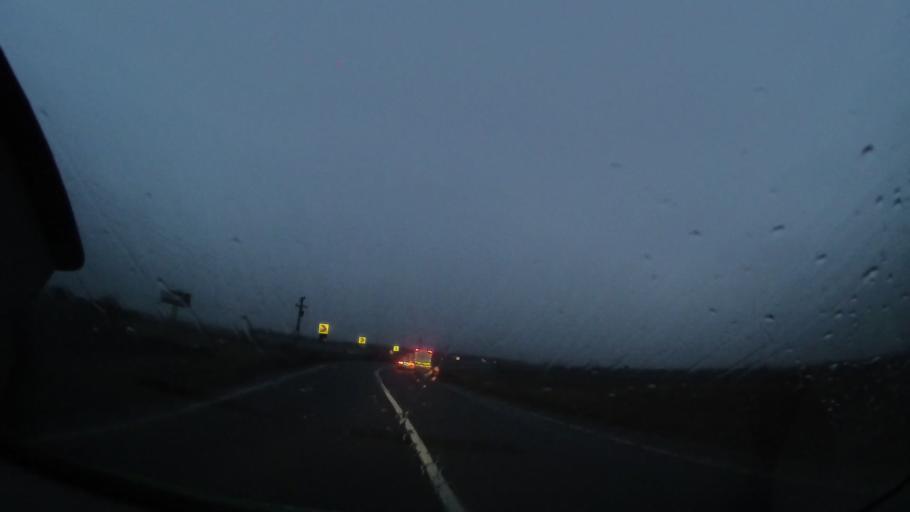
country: RO
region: Harghita
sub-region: Comuna Ditrau
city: Ditrau
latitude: 46.8179
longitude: 25.4922
